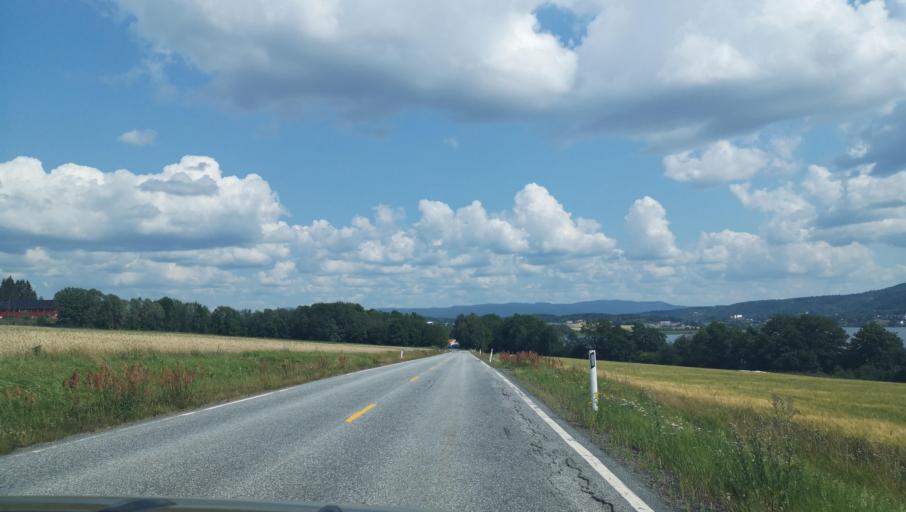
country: NO
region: Buskerud
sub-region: Ovre Eiker
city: Hokksund
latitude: 59.7066
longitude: 9.8117
